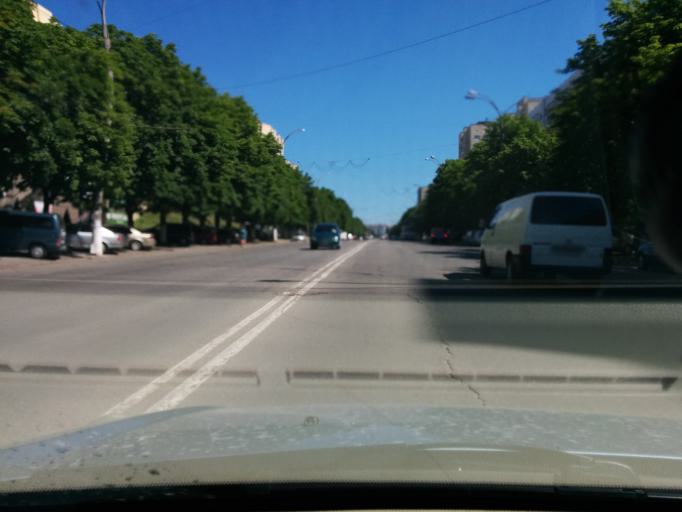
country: MD
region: Chisinau
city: Stauceni
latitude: 47.0513
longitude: 28.8641
